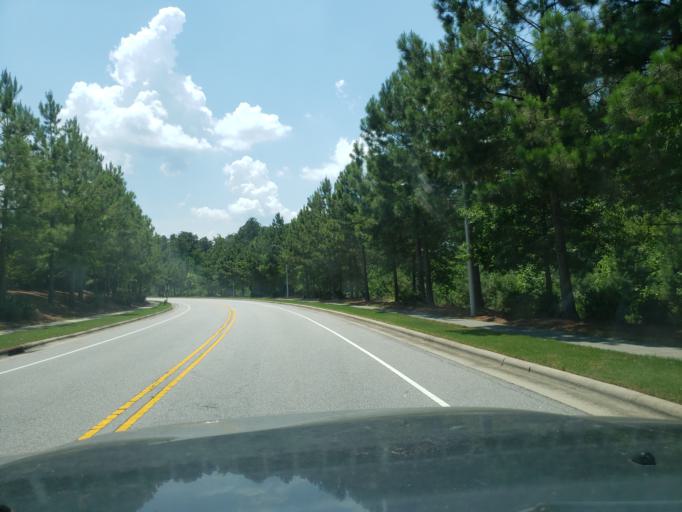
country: US
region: North Carolina
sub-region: Wake County
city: Green Level
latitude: 35.8421
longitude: -78.9146
